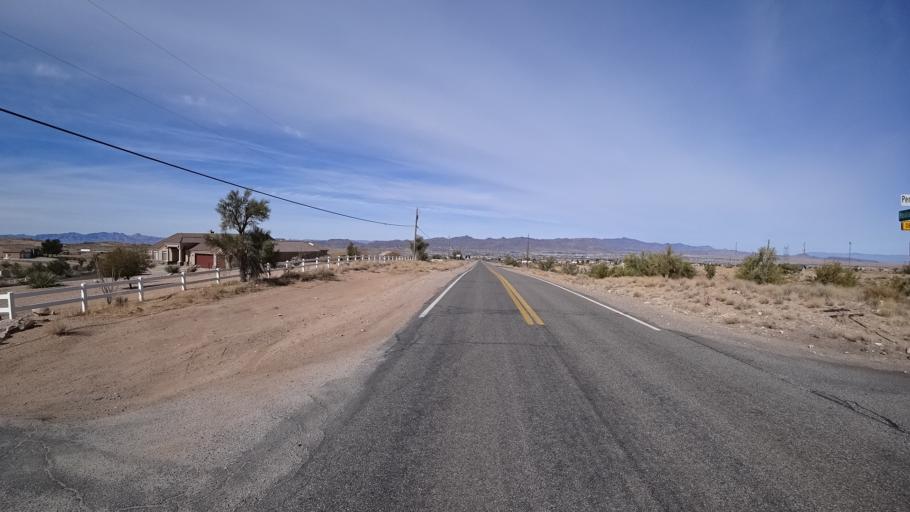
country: US
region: Arizona
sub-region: Mohave County
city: Kingman
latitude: 35.1715
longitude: -113.9817
